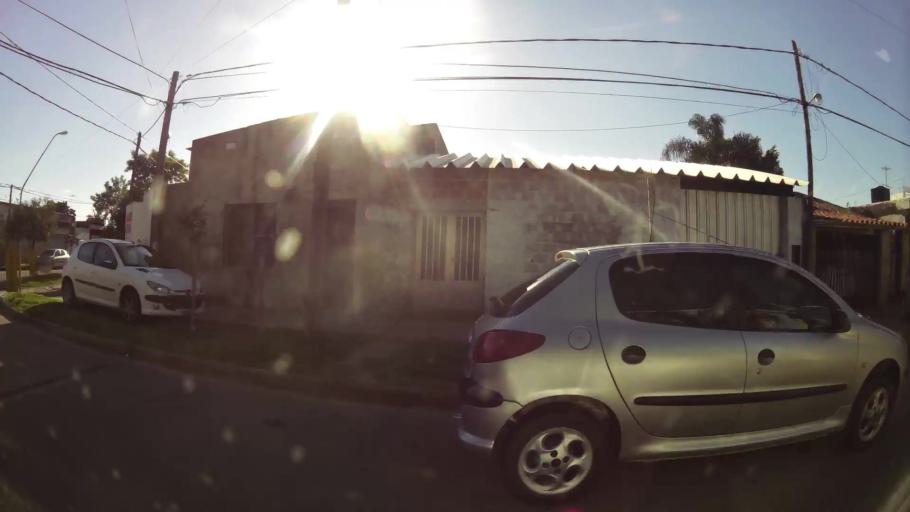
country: AR
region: Santa Fe
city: Santa Fe de la Vera Cruz
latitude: -31.6103
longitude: -60.6958
